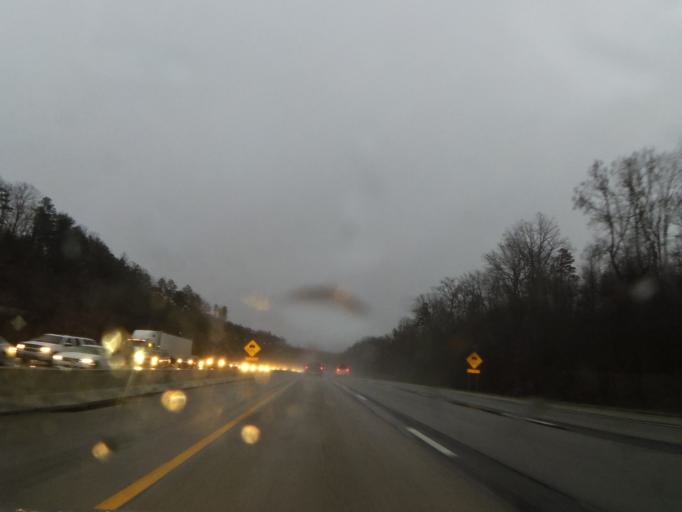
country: US
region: Kentucky
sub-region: Rockcastle County
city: Mount Vernon
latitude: 37.2842
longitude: -84.2621
